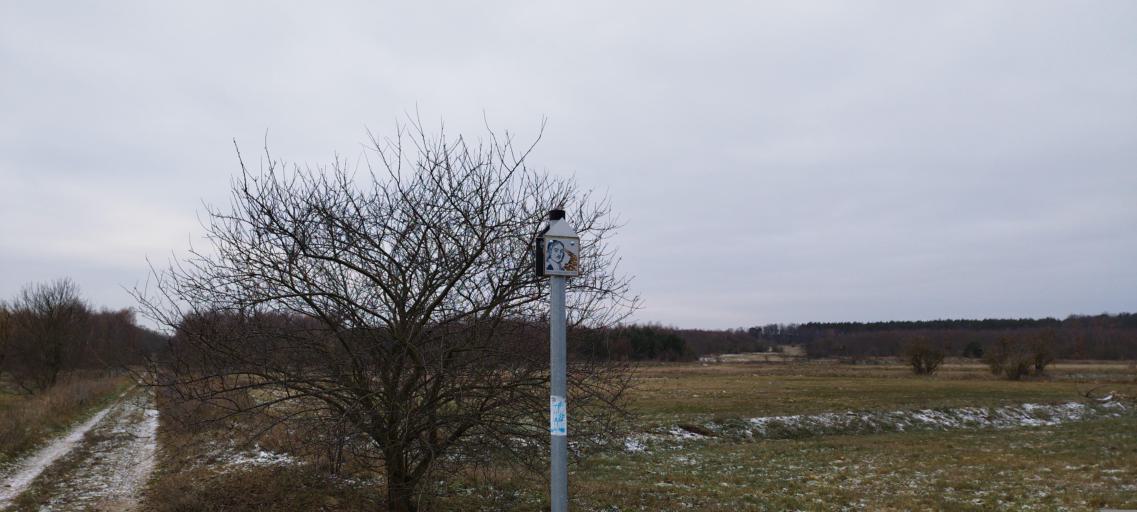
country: DE
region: Brandenburg
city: Schulzendorf
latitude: 52.3131
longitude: 13.5661
